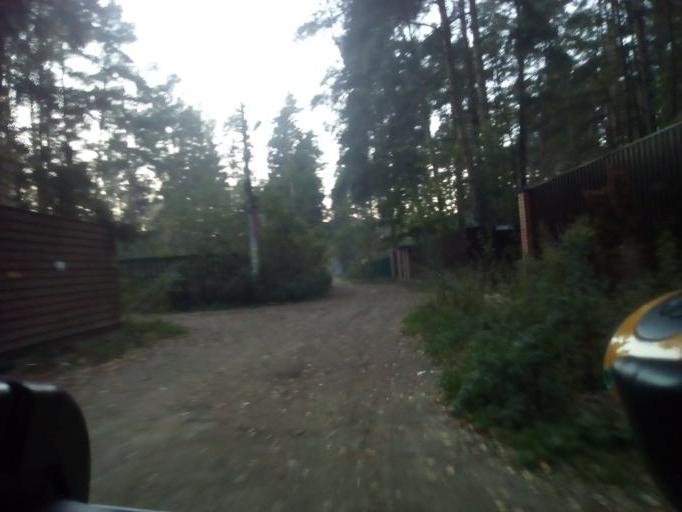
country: RU
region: Moskovskaya
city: Kratovo
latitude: 55.6067
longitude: 38.1693
